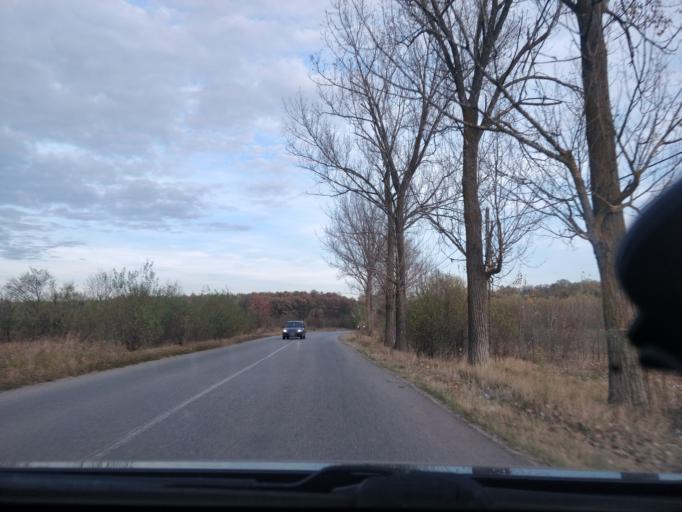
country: RO
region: Giurgiu
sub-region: Comuna Crevedia Mare
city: Crevedia Mare
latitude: 44.4319
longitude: 25.6573
